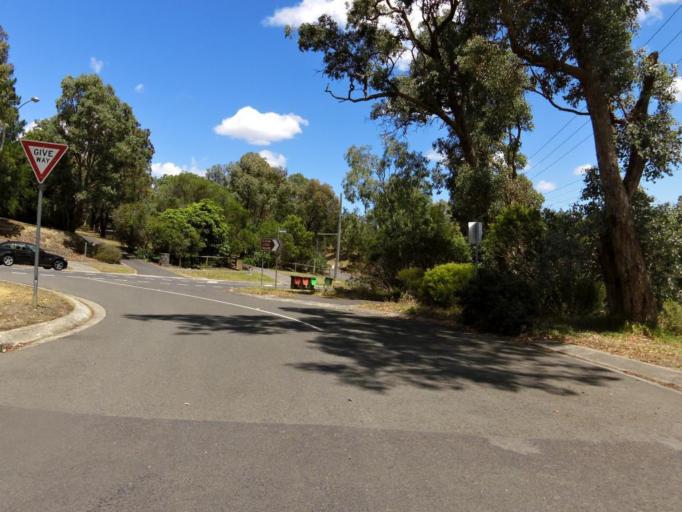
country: AU
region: Victoria
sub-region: Nillumbik
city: Research
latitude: -37.7017
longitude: 145.1856
